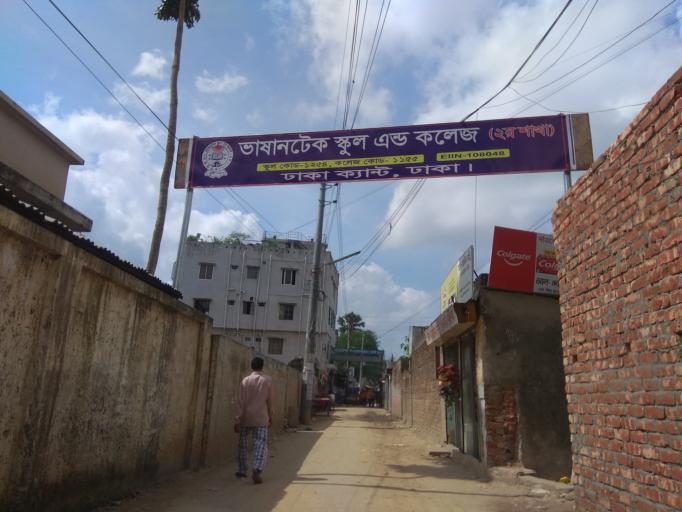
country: BD
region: Dhaka
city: Tungi
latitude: 23.8134
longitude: 90.3923
